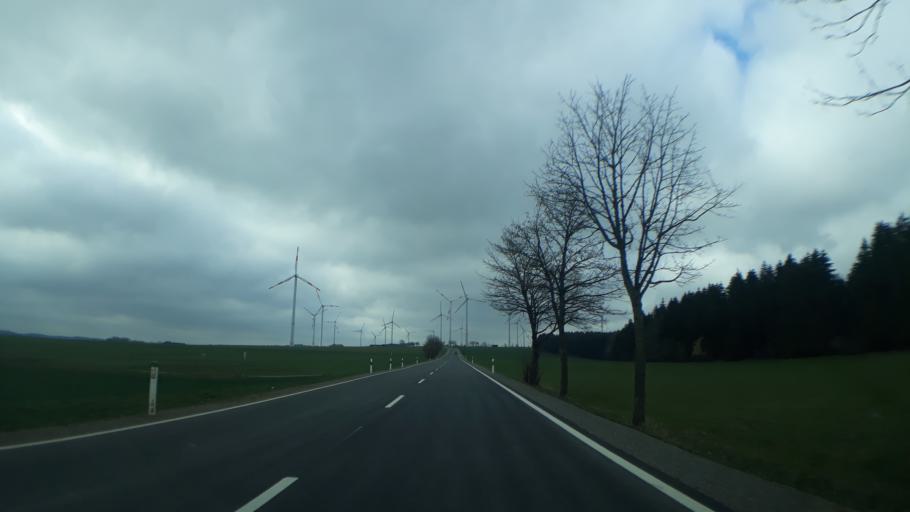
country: DE
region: North Rhine-Westphalia
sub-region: Regierungsbezirk Koln
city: Hellenthal
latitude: 50.5291
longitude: 6.3869
